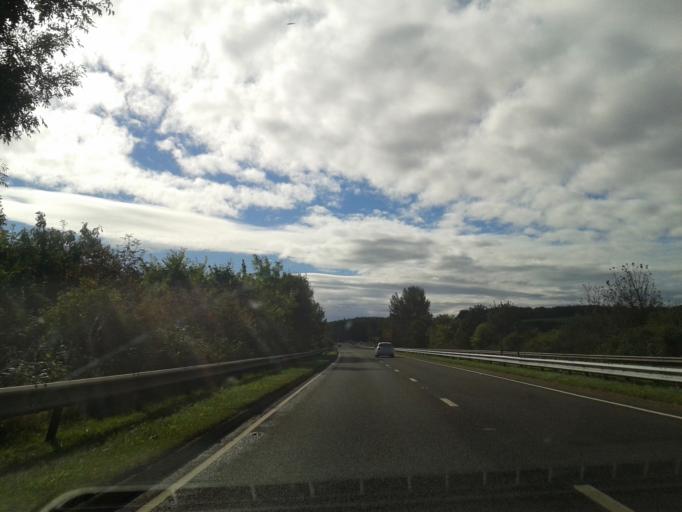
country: GB
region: Scotland
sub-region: Fife
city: Newport-On-Tay
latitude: 56.4344
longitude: -2.9336
